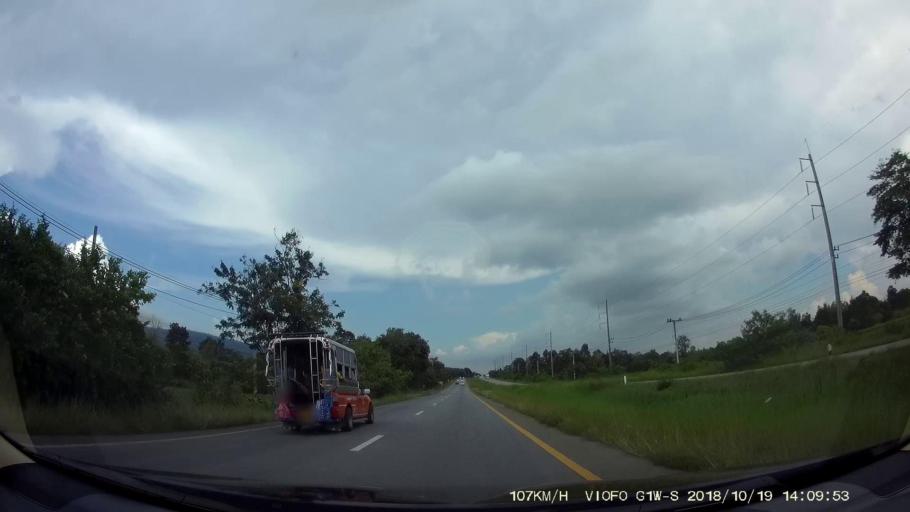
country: TH
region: Chaiyaphum
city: Khon Sawan
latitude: 15.9243
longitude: 102.1399
